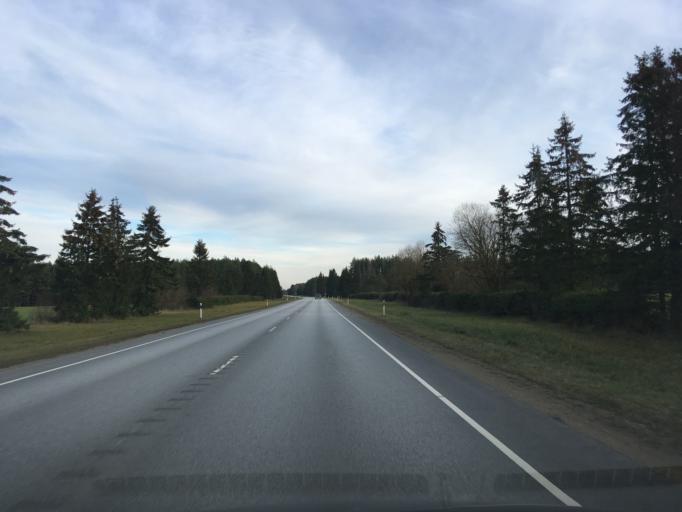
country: EE
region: Laeaene-Virumaa
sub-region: Viru-Nigula vald
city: Kunda
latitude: 59.3916
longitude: 26.6201
